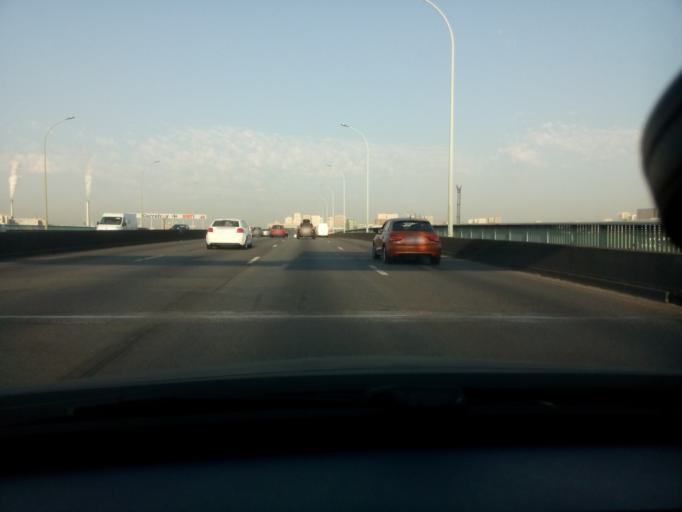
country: FR
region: Ile-de-France
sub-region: Departement du Val-de-Marne
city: Charenton-le-Pont
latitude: 48.8289
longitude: 2.3992
